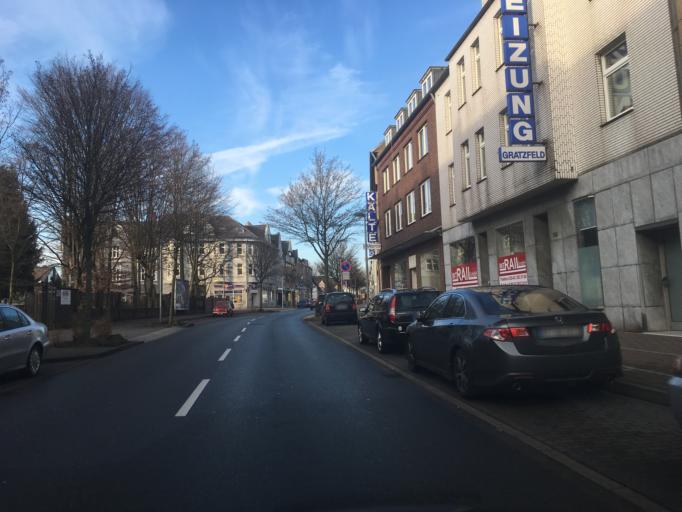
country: DE
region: North Rhine-Westphalia
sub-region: Regierungsbezirk Munster
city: Gladbeck
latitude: 51.5538
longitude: 7.0025
